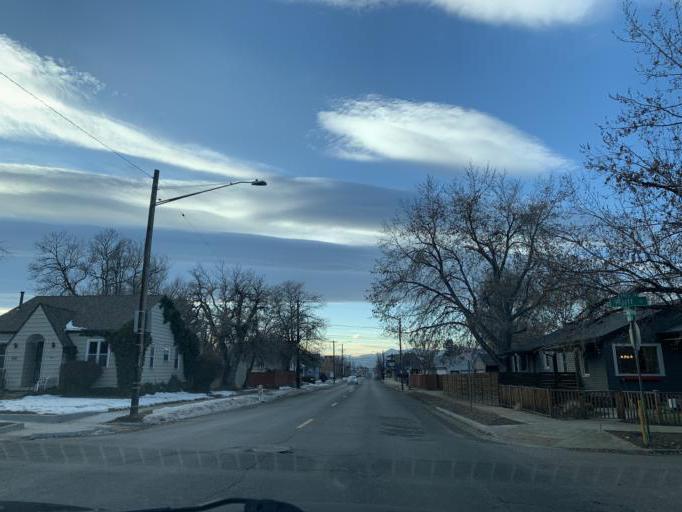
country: US
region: Colorado
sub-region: Jefferson County
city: Edgewater
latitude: 39.7766
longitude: -105.0485
